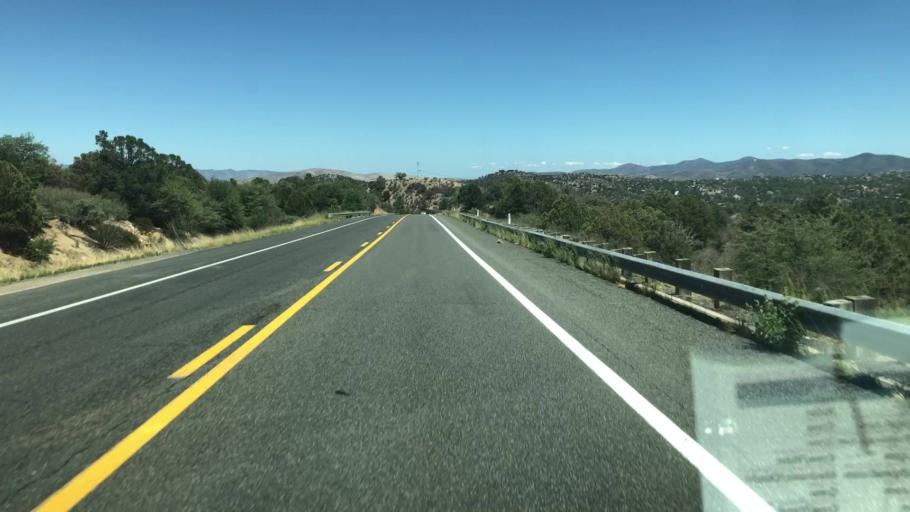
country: US
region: Arizona
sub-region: Yavapai County
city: Prescott
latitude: 34.5813
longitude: -112.5360
